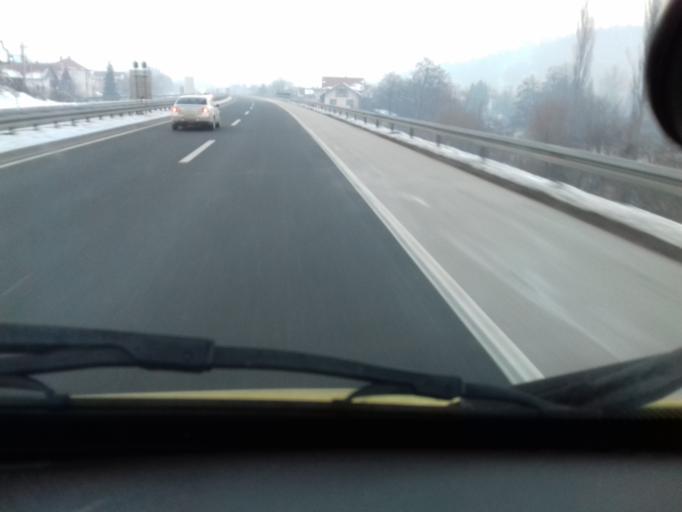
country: BA
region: Federation of Bosnia and Herzegovina
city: Vogosca
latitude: 43.9152
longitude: 18.3174
